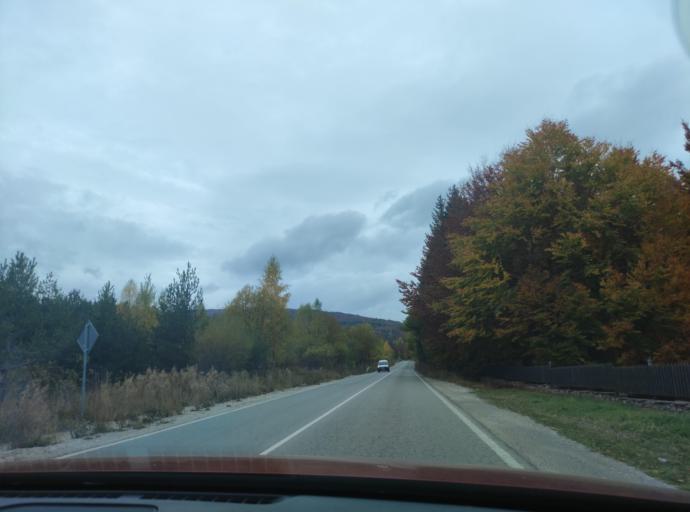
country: BG
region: Sofiya
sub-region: Obshtina Godech
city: Godech
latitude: 43.0991
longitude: 23.1011
